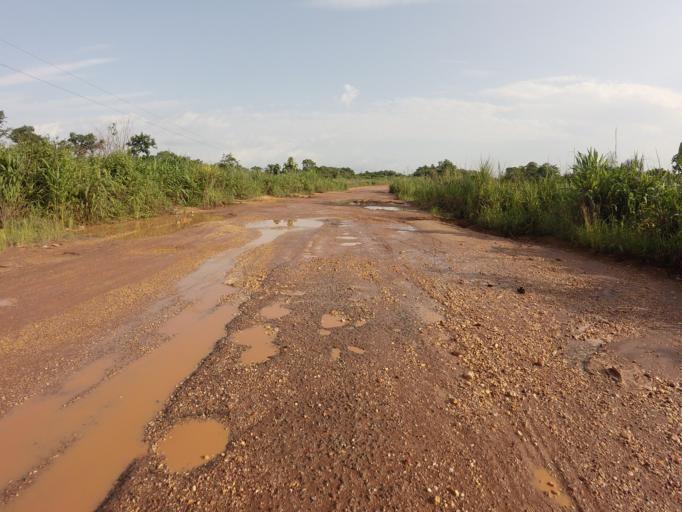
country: GH
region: Volta
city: Hohoe
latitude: 7.0858
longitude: 0.4448
